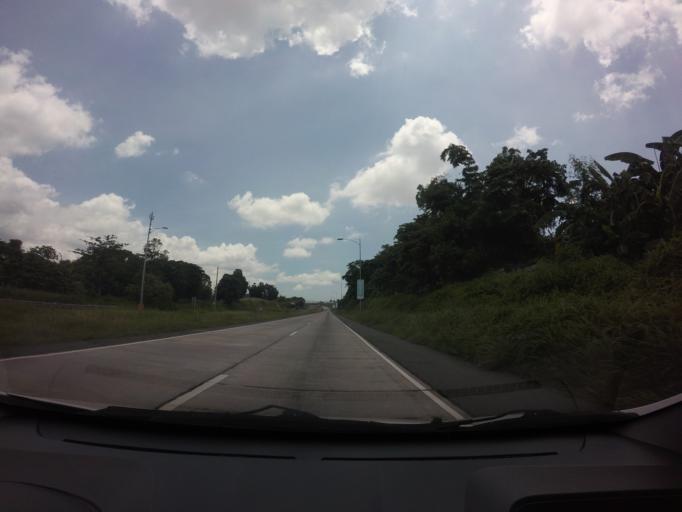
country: PH
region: Calabarzon
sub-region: Province of Laguna
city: San Pedro
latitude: 14.3771
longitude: 121.0266
